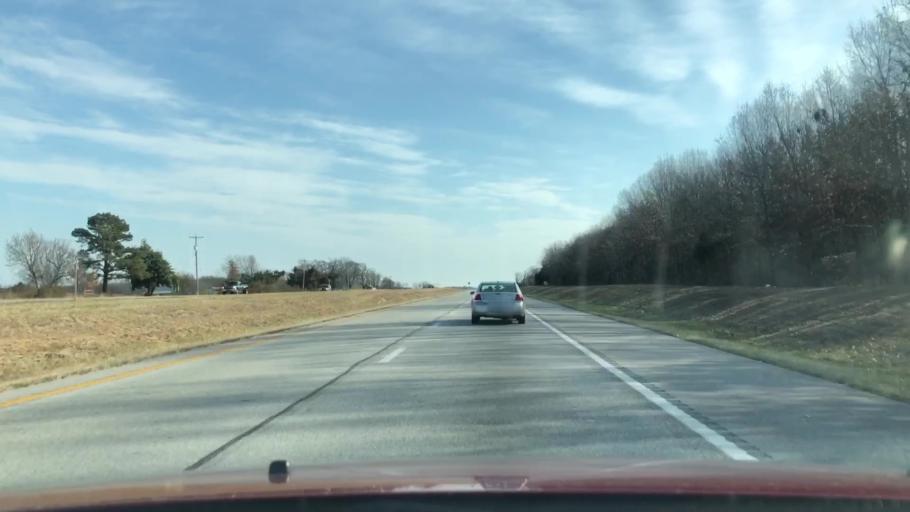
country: US
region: Missouri
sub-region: Christian County
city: Ozark
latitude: 37.1196
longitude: -93.1693
